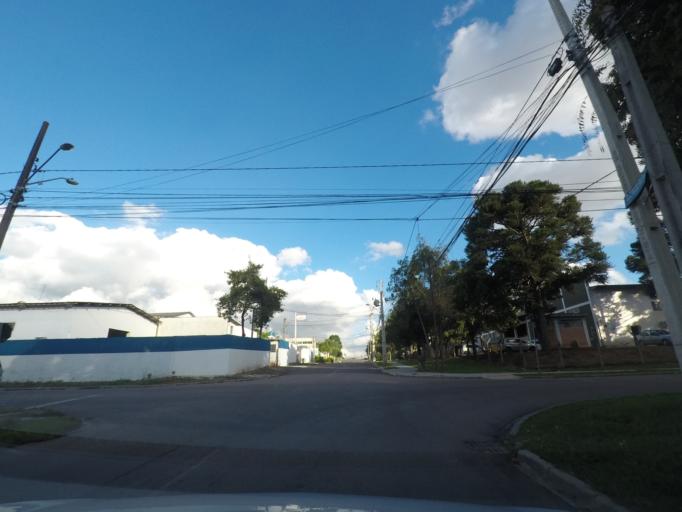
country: BR
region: Parana
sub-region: Curitiba
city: Curitiba
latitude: -25.4838
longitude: -49.2615
